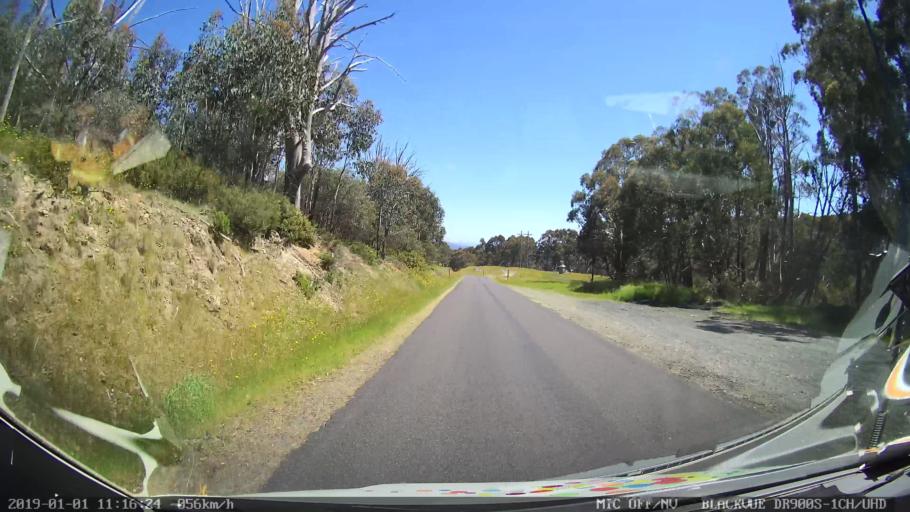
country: AU
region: New South Wales
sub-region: Snowy River
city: Jindabyne
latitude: -35.9394
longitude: 148.3857
